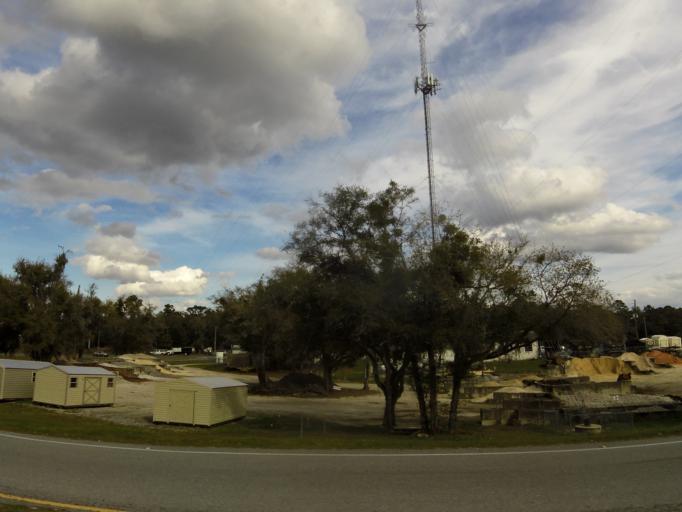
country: US
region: Florida
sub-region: Volusia County
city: Orange City
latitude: 28.9762
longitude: -81.3007
